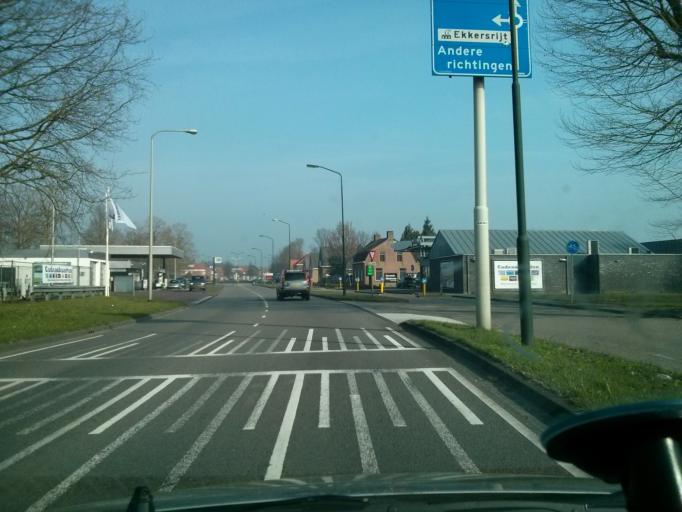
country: NL
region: North Brabant
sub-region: Gemeente Son en Breugel
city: Son
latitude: 51.5005
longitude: 5.4952
